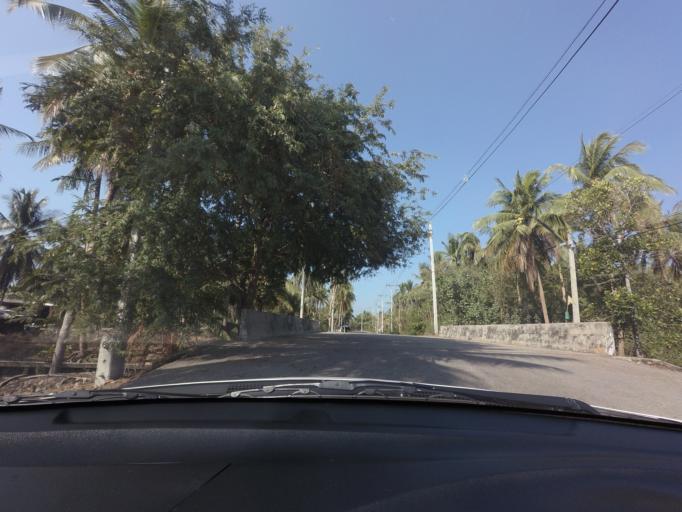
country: TH
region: Ratchaburi
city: Damnoen Saduak
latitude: 13.4839
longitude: 100.0030
